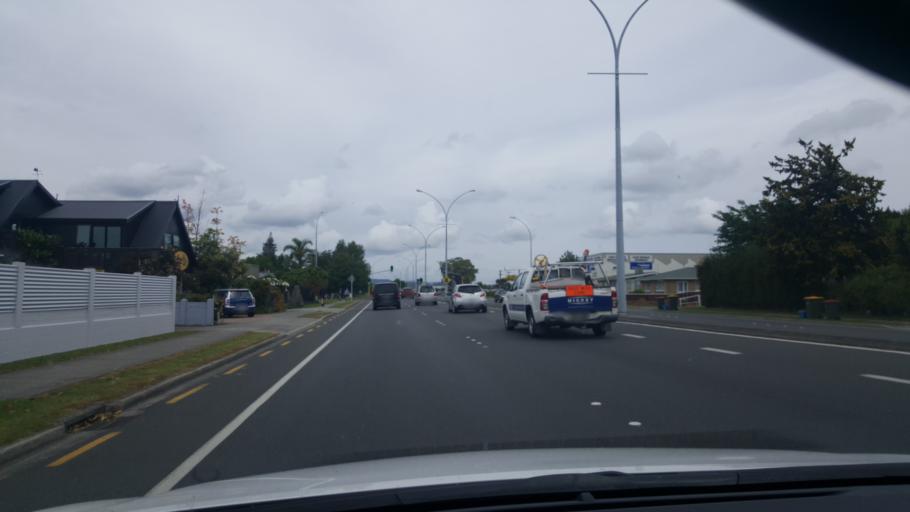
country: NZ
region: Bay of Plenty
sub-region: Rotorua District
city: Rotorua
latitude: -38.1142
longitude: 176.2256
